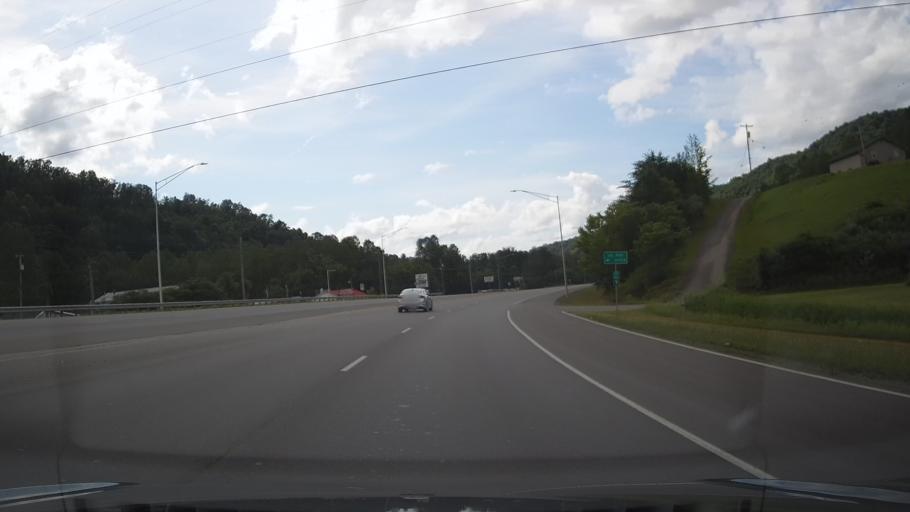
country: US
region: Kentucky
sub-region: Floyd County
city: Prestonsburg
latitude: 37.6040
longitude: -82.6998
